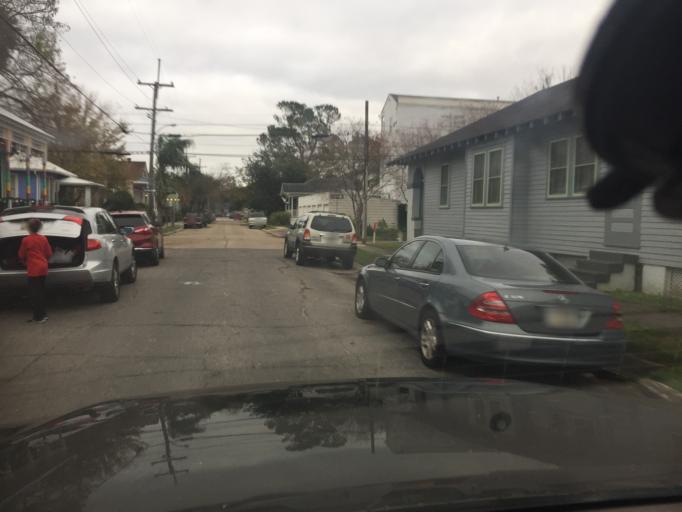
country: US
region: Louisiana
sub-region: Orleans Parish
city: New Orleans
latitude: 29.9803
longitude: -90.0802
